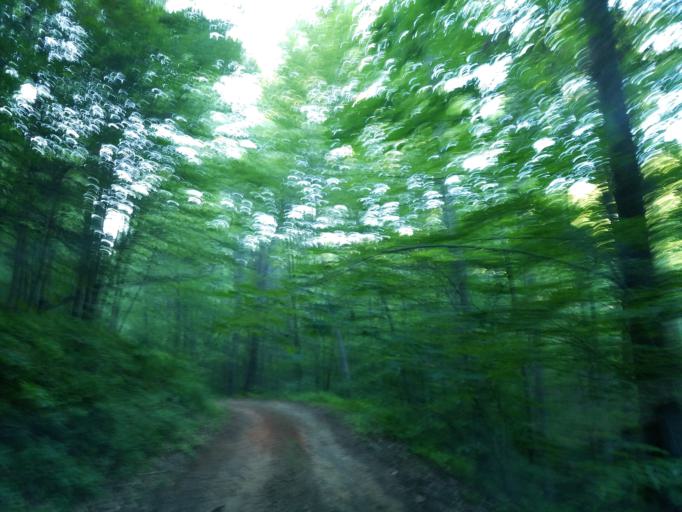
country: US
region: Georgia
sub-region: Fannin County
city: Blue Ridge
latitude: 34.8055
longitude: -84.1700
